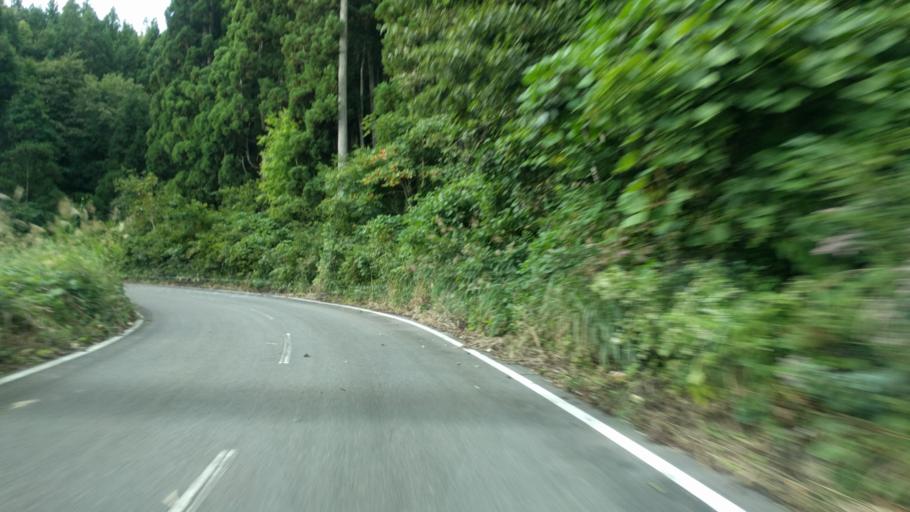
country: JP
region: Fukushima
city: Kitakata
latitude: 37.5003
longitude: 139.7700
